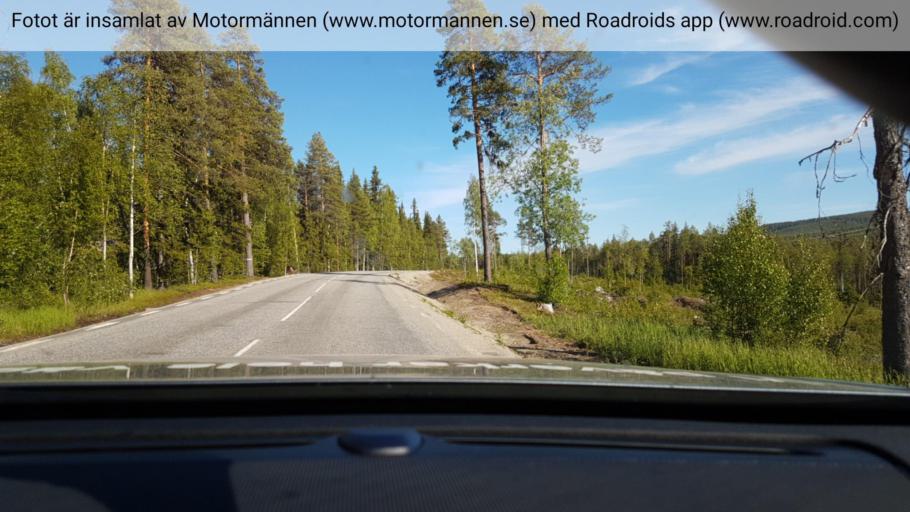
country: SE
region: Vaesterbotten
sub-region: Norsjo Kommun
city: Norsjoe
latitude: 64.6943
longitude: 19.1906
